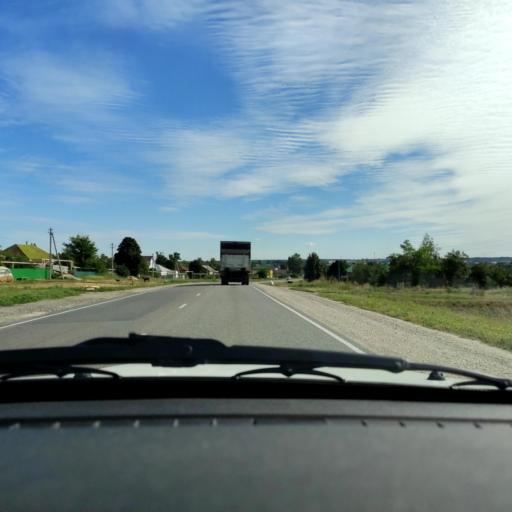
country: RU
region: Voronezj
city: Orlovo
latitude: 51.7467
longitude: 39.5813
